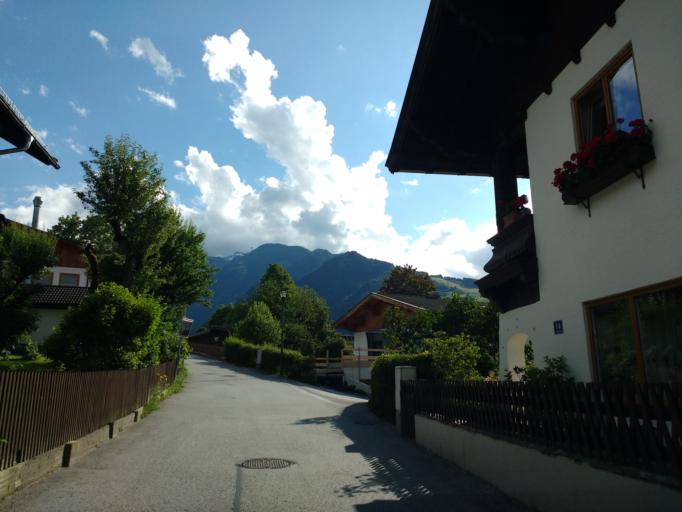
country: AT
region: Salzburg
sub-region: Politischer Bezirk Zell am See
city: Kaprun
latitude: 47.2712
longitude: 12.7619
